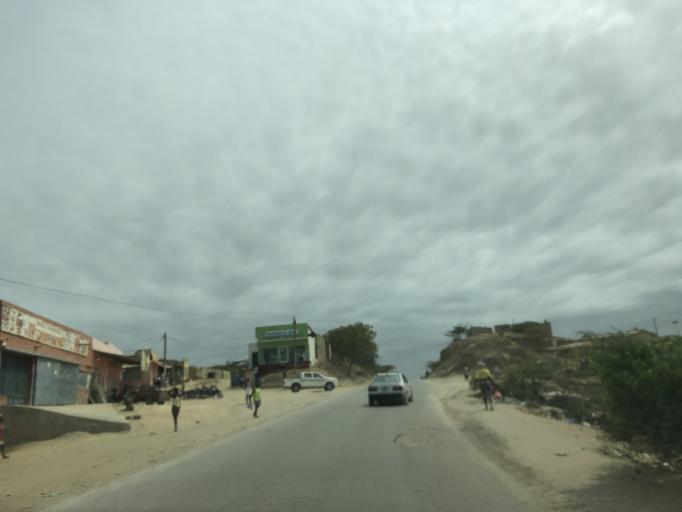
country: AO
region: Cuanza Sul
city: Sumbe
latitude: -11.2259
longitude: 13.8446
